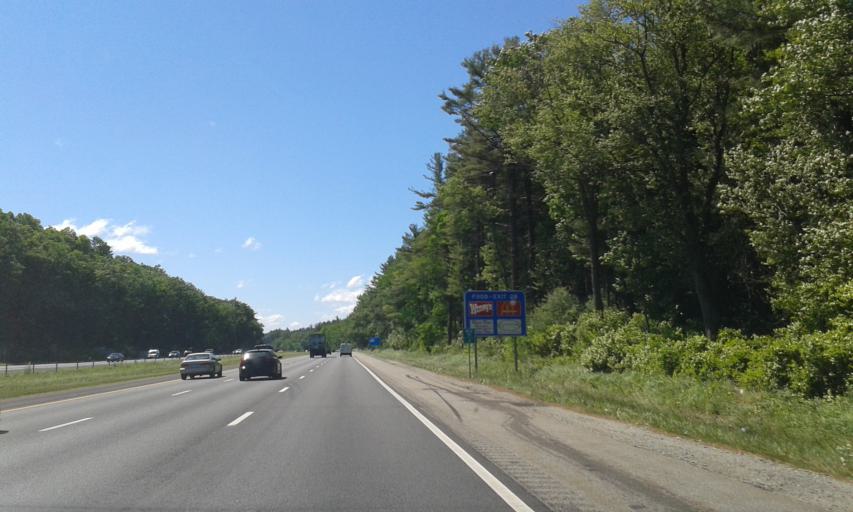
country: US
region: Massachusetts
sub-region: Middlesex County
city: Billerica
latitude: 42.5710
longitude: -71.3040
